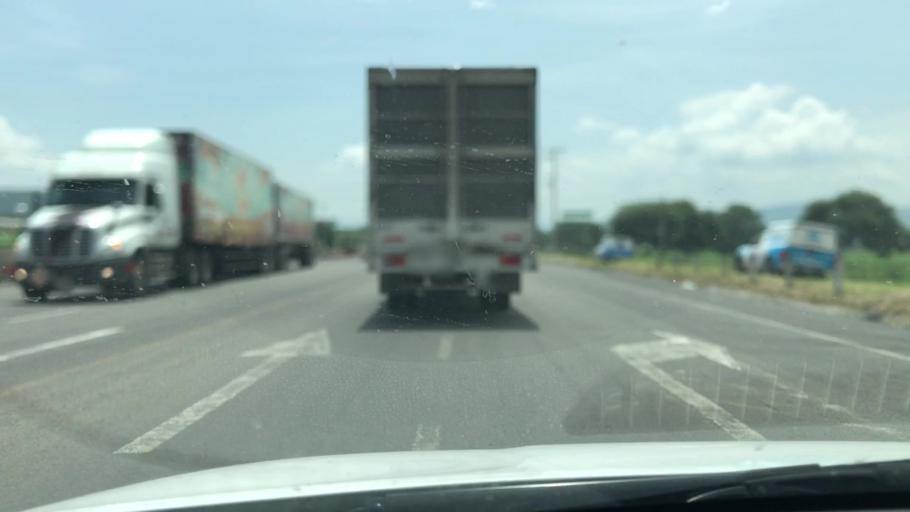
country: MX
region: Michoacan
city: Vistahermosa de Negrete
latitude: 20.2689
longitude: -102.4442
